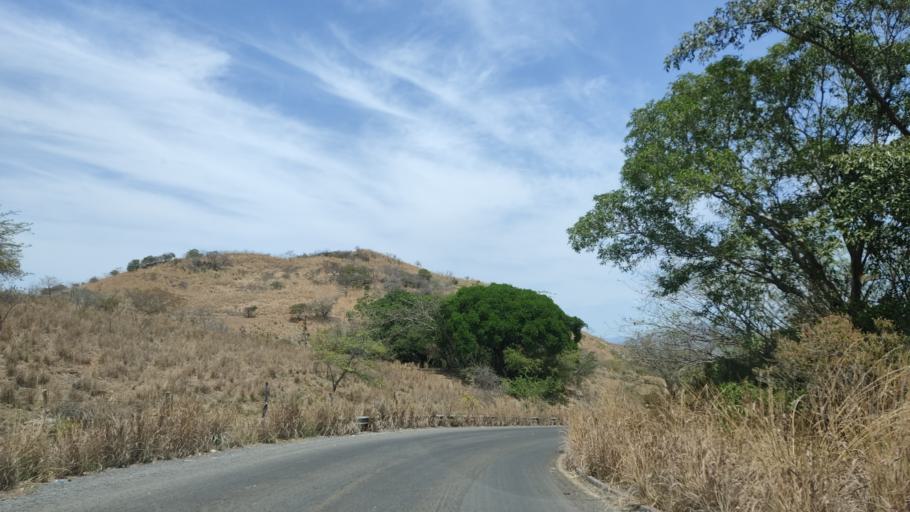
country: MX
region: Nayarit
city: Santa Maria del Oro
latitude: 21.5026
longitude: -104.6160
